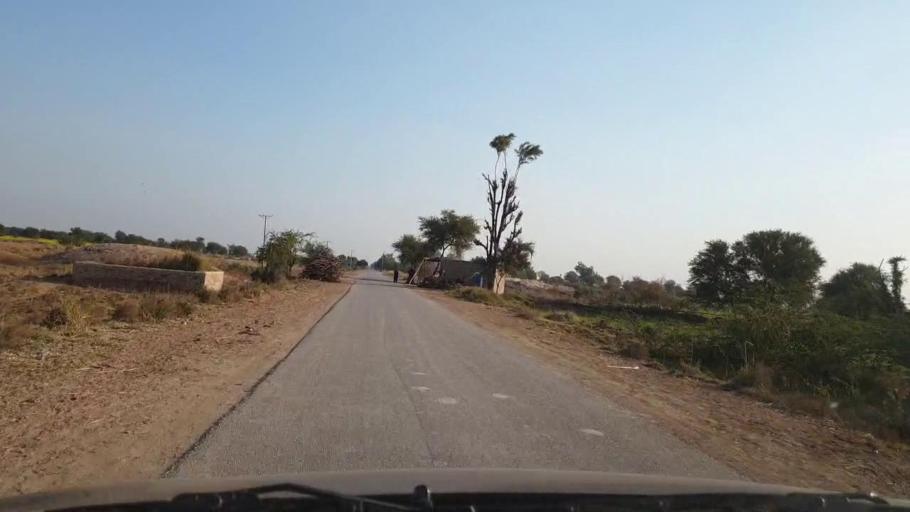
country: PK
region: Sindh
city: Jhol
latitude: 25.9566
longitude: 68.8971
